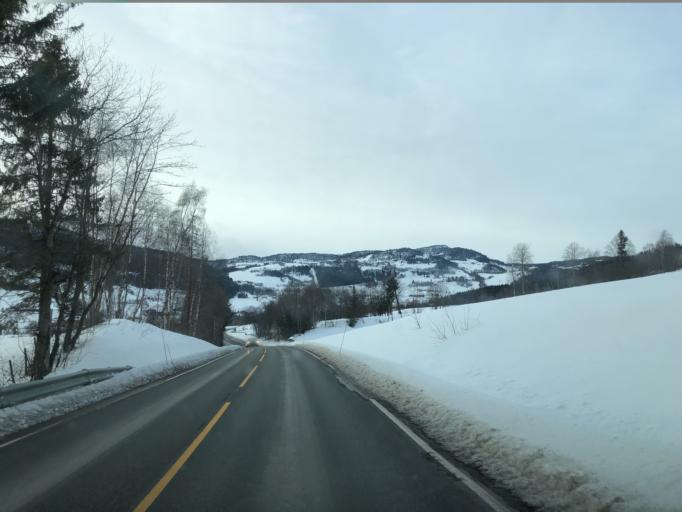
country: NO
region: Oppland
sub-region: Gausdal
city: Segalstad bru
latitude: 61.2600
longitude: 10.1660
